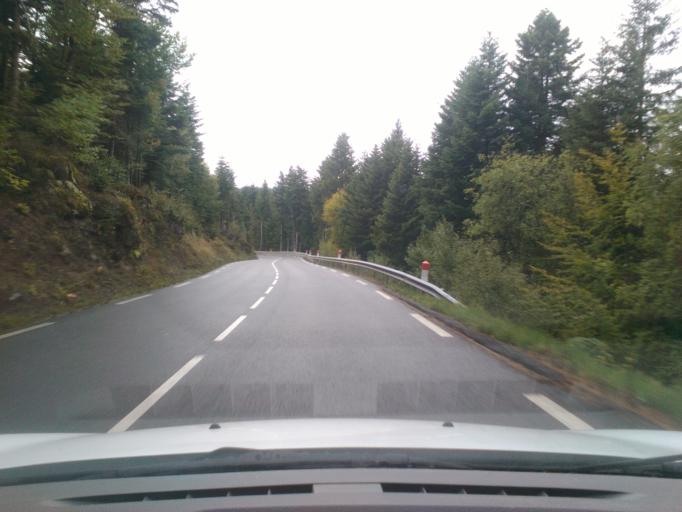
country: FR
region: Lorraine
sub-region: Departement des Vosges
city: Taintrux
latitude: 48.2759
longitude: 6.8514
